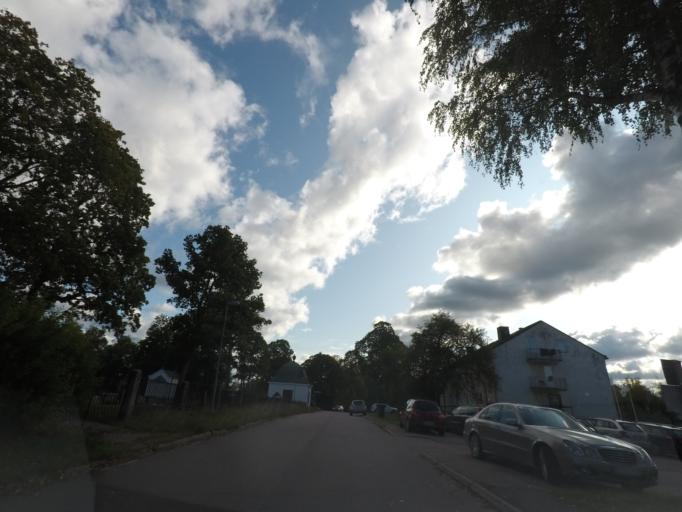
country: SE
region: Vaestmanland
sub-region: Skinnskattebergs Kommun
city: Skinnskatteberg
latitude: 59.8300
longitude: 15.6826
